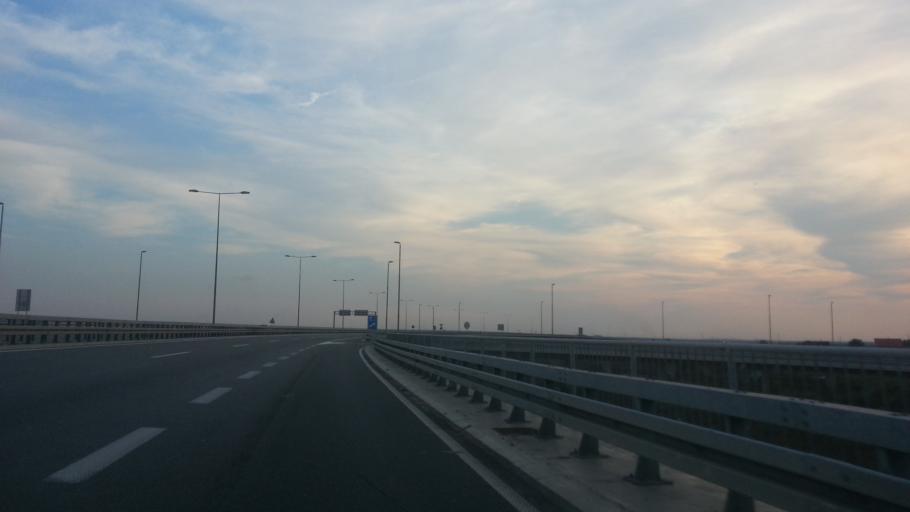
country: RS
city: Novi Banovci
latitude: 44.8921
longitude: 20.2971
